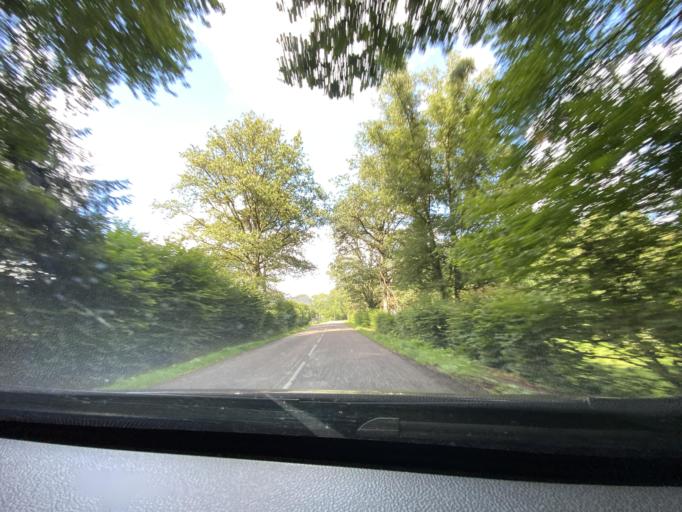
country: FR
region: Bourgogne
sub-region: Departement de la Cote-d'Or
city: Saulieu
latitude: 47.2725
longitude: 4.1274
